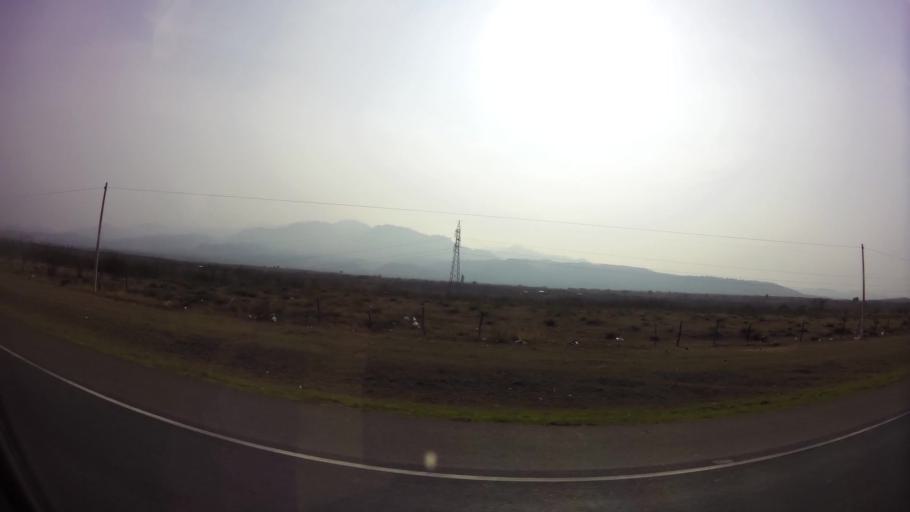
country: HN
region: Comayagua
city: Comayagua
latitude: 14.4035
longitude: -87.6193
